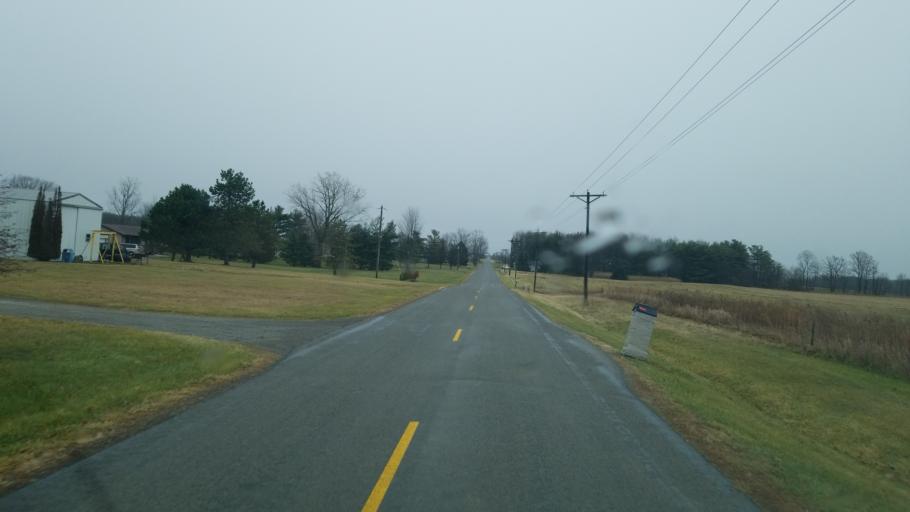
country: US
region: Ohio
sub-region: Logan County
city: Northwood
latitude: 40.4476
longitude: -83.6173
